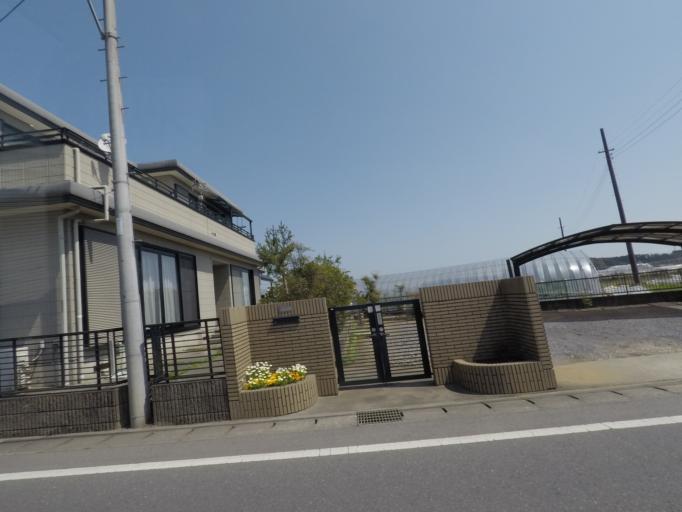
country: JP
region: Chiba
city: Yokaichiba
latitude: 35.7017
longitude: 140.4555
